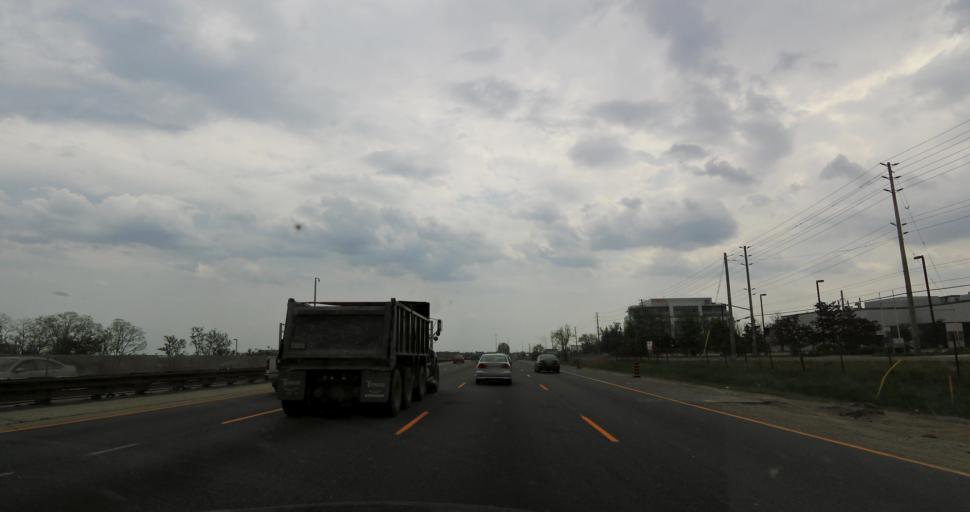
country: CA
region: Ontario
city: Oakville
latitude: 43.4826
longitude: -79.6729
